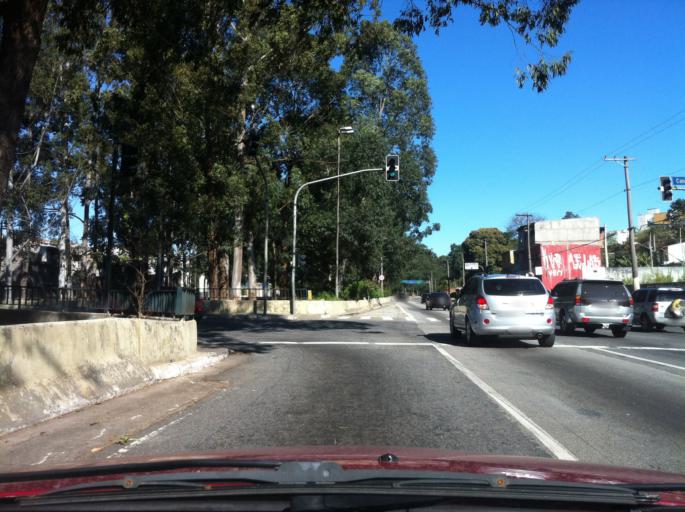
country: BR
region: Sao Paulo
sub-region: Ferraz De Vasconcelos
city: Ferraz de Vasconcelos
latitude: -23.5454
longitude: -46.4473
